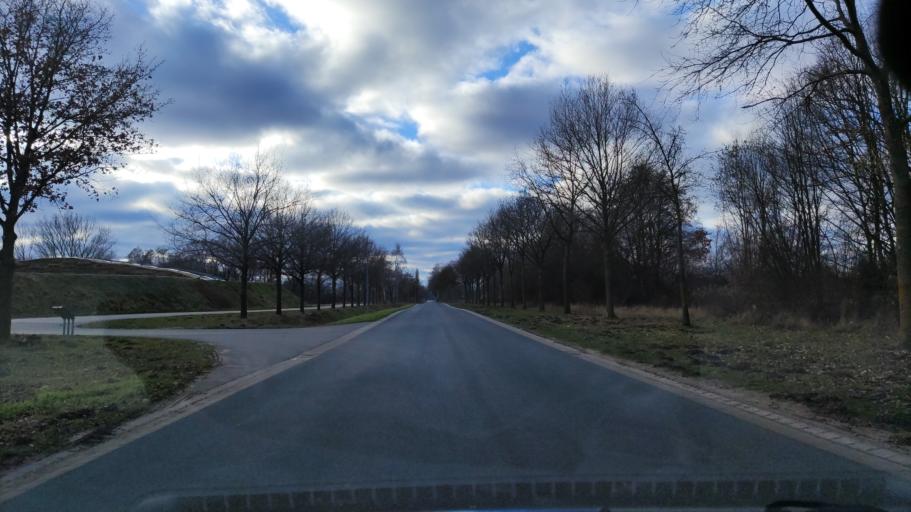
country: DE
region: Lower Saxony
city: Dannenberg
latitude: 53.1068
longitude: 11.1287
